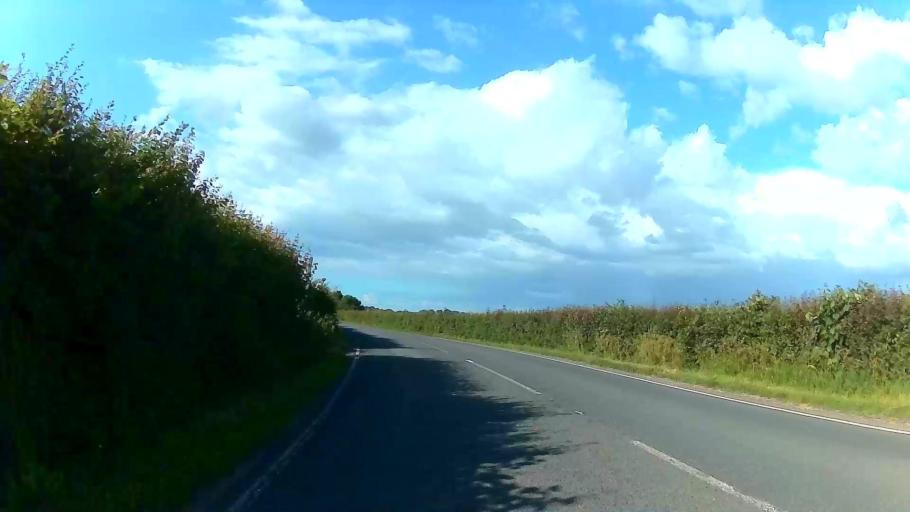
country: GB
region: England
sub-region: Essex
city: Kelvedon Hatch
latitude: 51.6845
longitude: 0.3071
